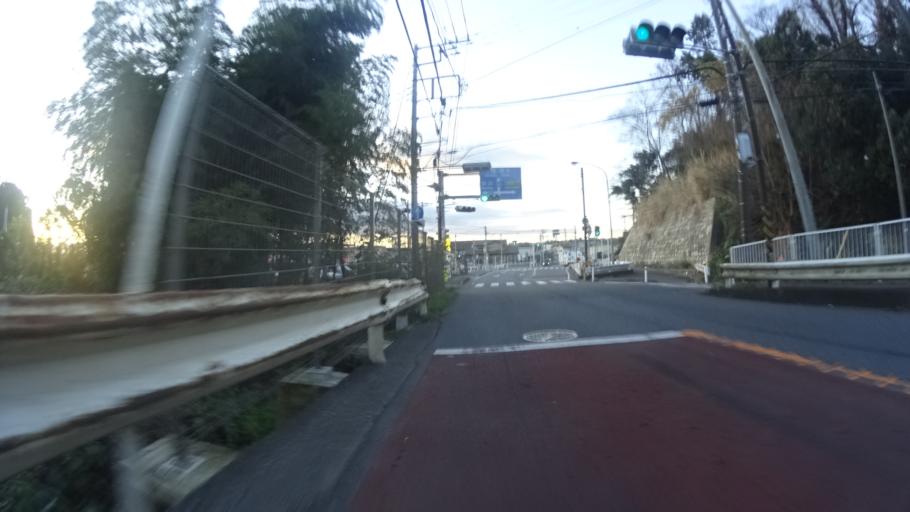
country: JP
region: Kanagawa
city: Zama
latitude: 35.5278
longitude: 139.3651
